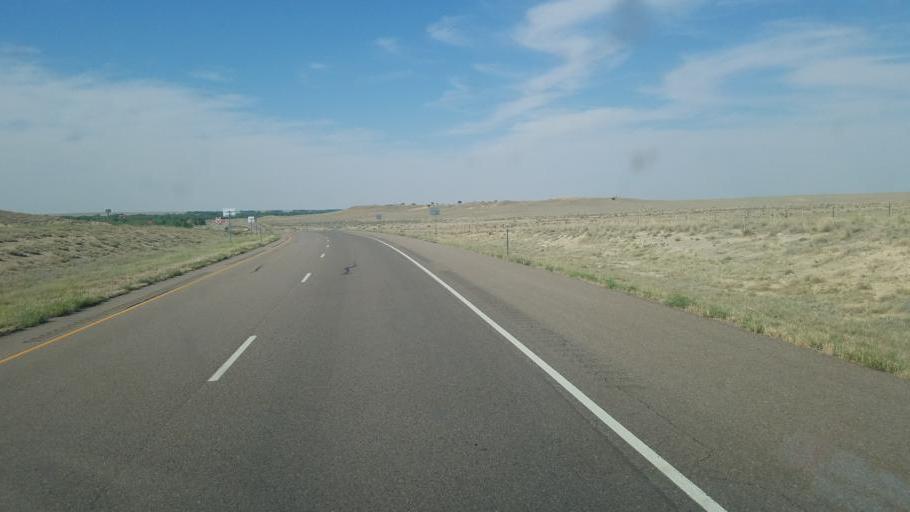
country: US
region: Colorado
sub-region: Otero County
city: La Junta
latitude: 38.0128
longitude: -103.4506
